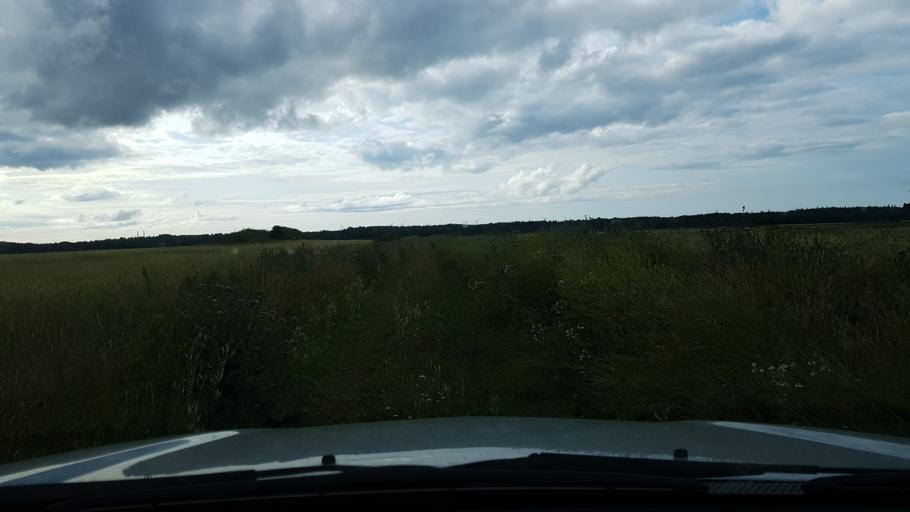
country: EE
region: Ida-Virumaa
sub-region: Narva-Joesuu linn
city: Narva-Joesuu
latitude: 59.3885
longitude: 27.9953
